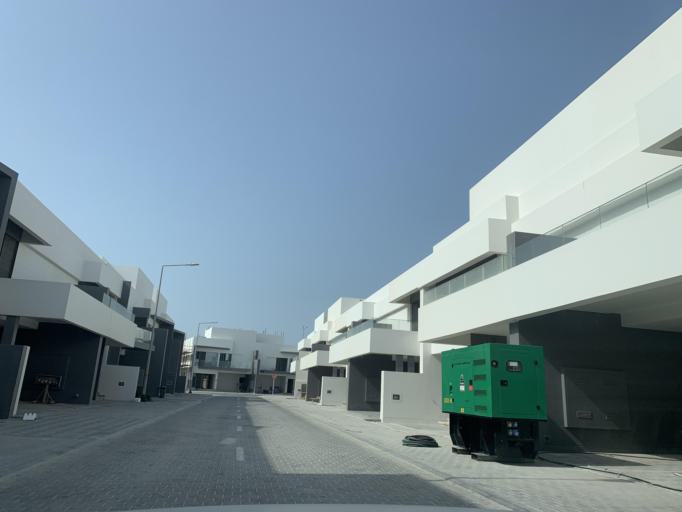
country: BH
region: Muharraq
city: Al Muharraq
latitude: 26.3113
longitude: 50.6364
